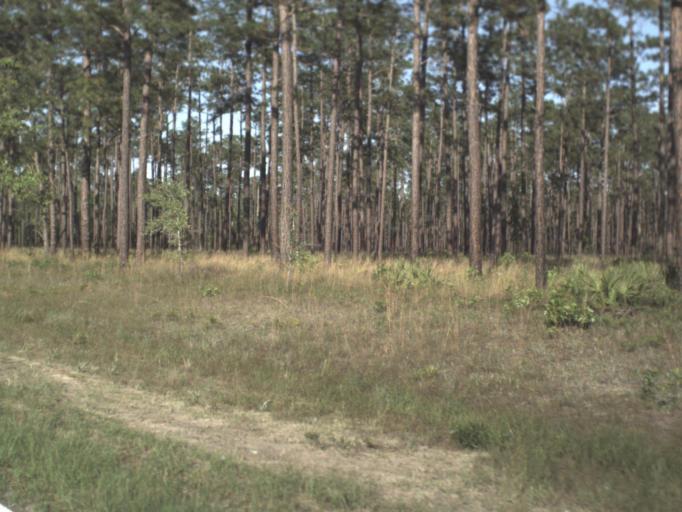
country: US
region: Florida
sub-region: Liberty County
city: Bristol
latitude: 30.2106
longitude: -84.8993
